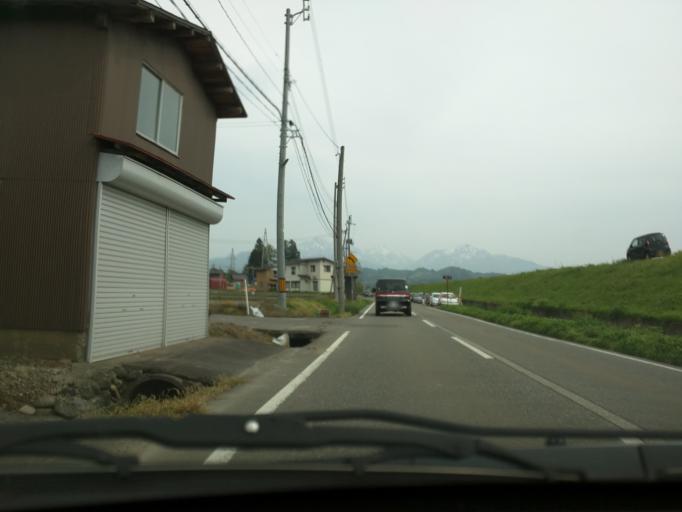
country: JP
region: Niigata
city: Ojiya
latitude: 37.2537
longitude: 138.9214
